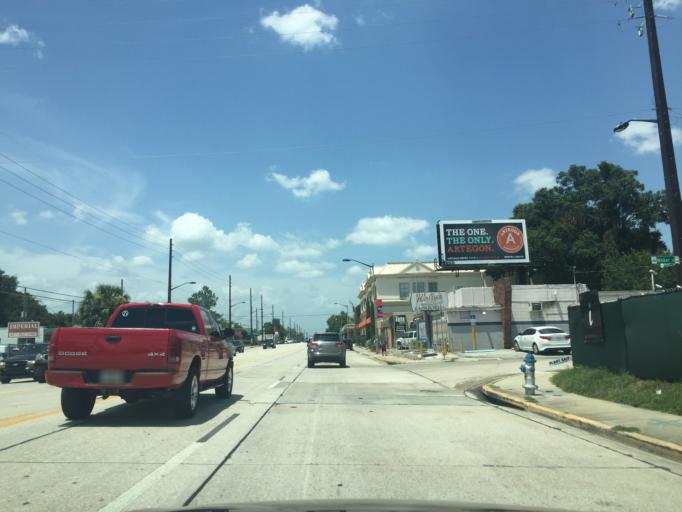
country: US
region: Florida
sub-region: Orange County
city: Orlando
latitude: 28.5583
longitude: -81.3644
